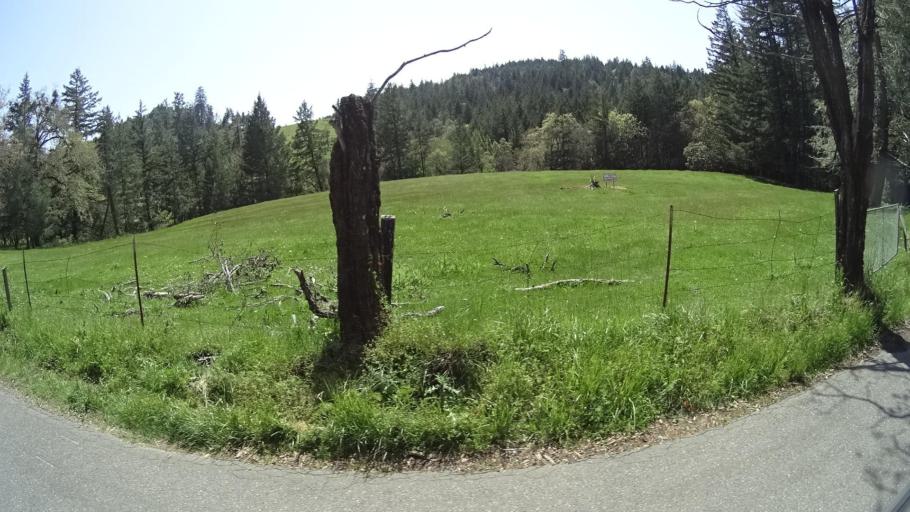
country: US
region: California
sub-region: Humboldt County
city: Redway
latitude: 40.2795
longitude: -123.6418
